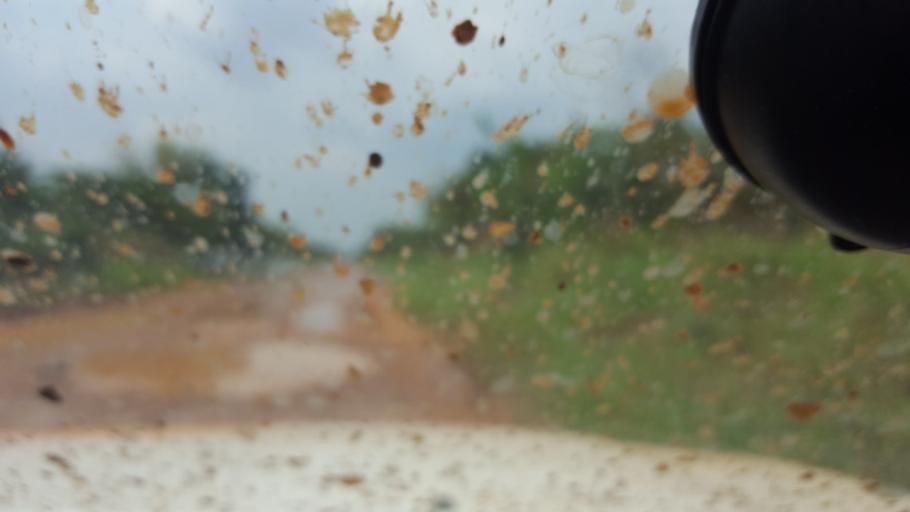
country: CD
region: Bandundu
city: Bandundu
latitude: -3.7617
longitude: 17.1511
